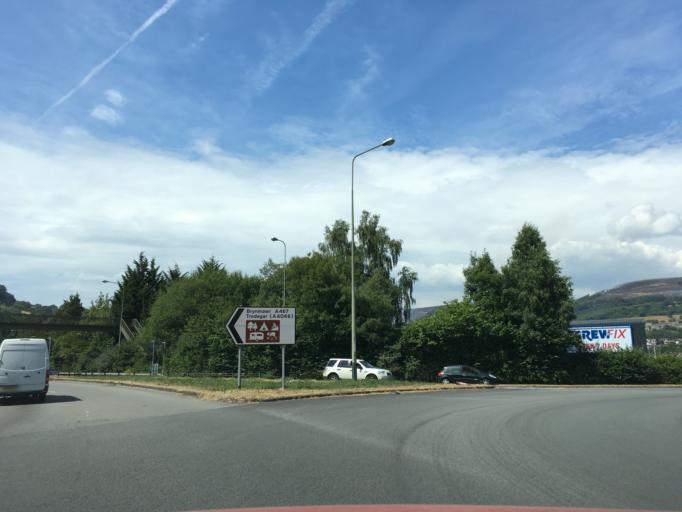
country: GB
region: Wales
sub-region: Caerphilly County Borough
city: Risca
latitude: 51.6004
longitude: -3.0938
